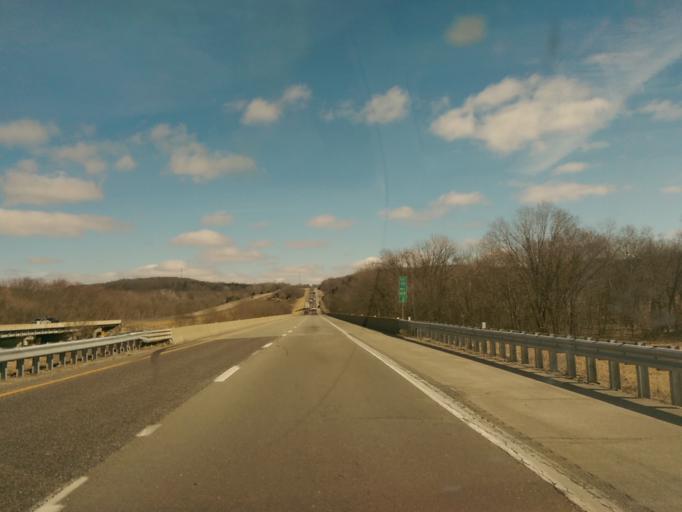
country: US
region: Missouri
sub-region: Montgomery County
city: Montgomery City
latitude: 38.8998
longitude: -91.5832
